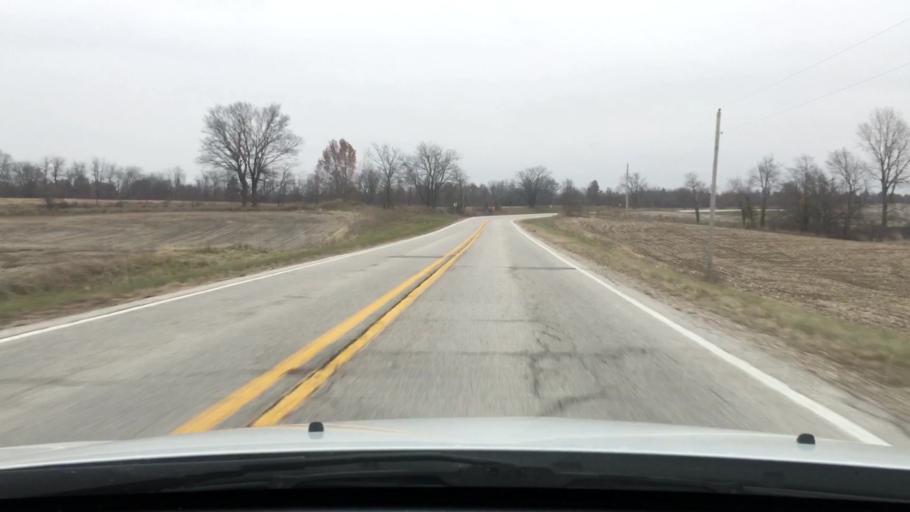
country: US
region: Illinois
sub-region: Pike County
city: Pittsfield
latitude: 39.5899
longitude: -90.8983
